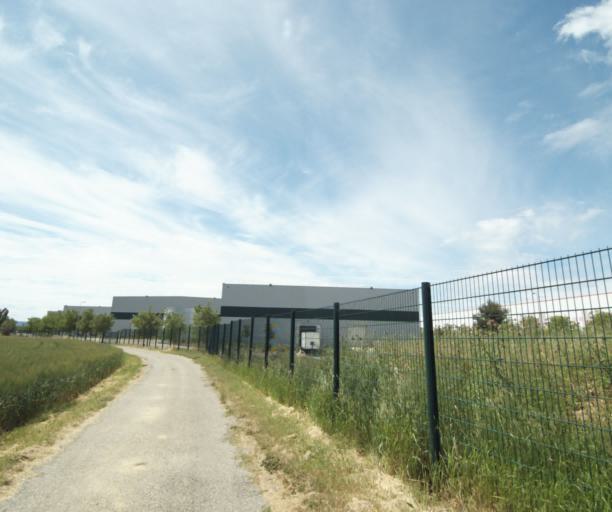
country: FR
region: Provence-Alpes-Cote d'Azur
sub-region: Departement des Bouches-du-Rhone
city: Rognac
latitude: 43.4985
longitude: 5.2215
